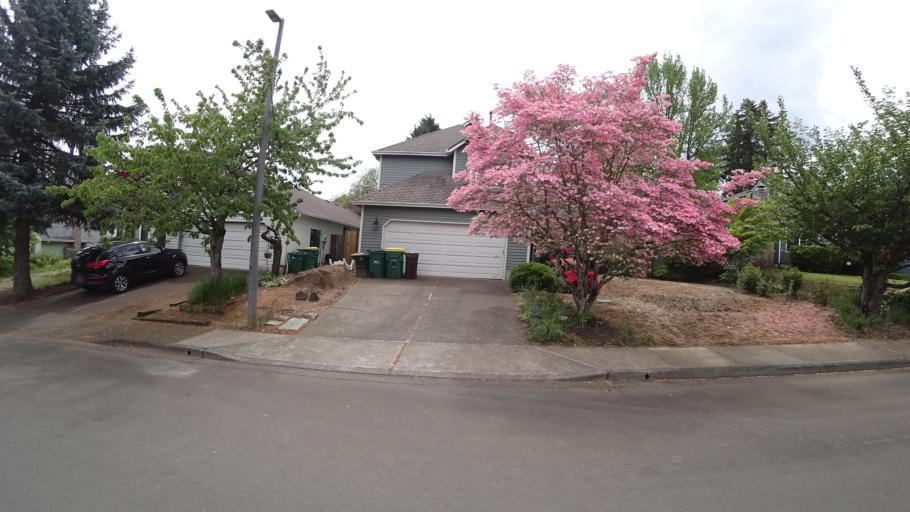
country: US
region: Oregon
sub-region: Washington County
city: Aloha
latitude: 45.4647
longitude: -122.8560
